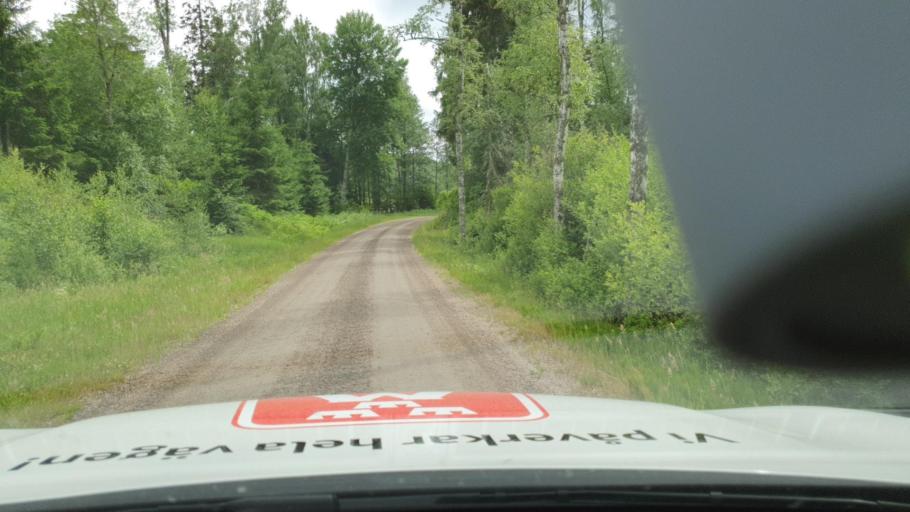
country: SE
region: Vaestra Goetaland
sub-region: Tidaholms Kommun
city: Olofstorp
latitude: 58.1775
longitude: 14.1029
